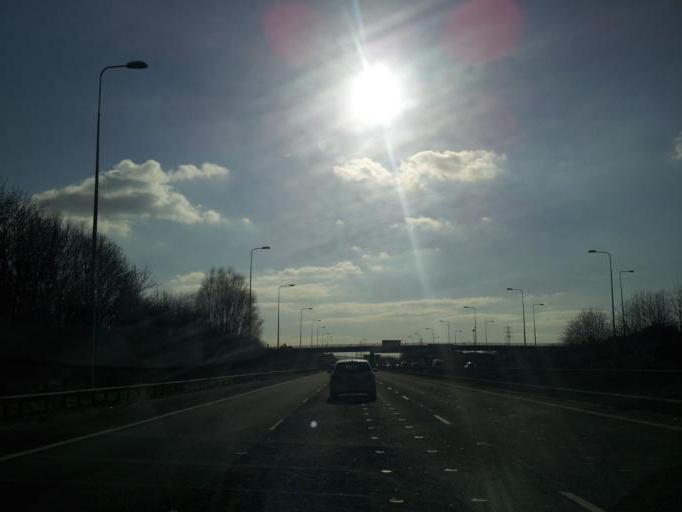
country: GB
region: England
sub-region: North Somerset
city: Easton-in-Gordano
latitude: 51.5043
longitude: -2.6691
